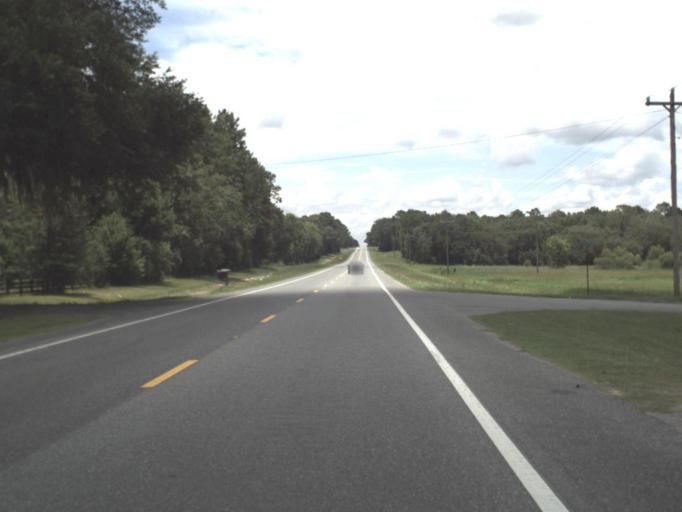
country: US
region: Florida
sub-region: Suwannee County
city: Live Oak
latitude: 30.2206
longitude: -82.9880
